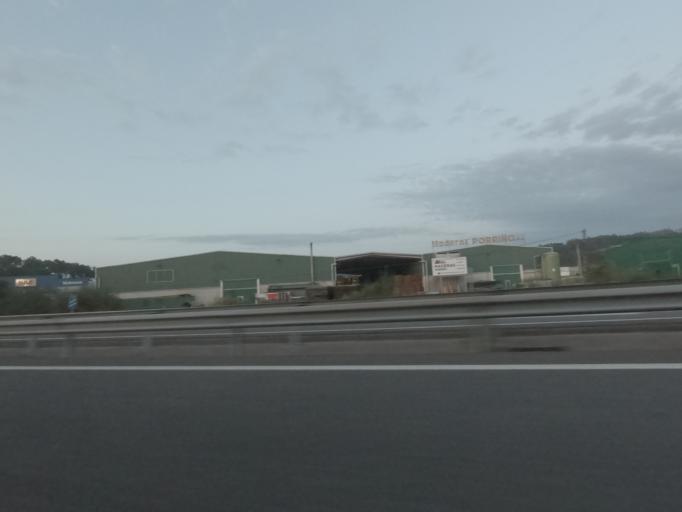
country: ES
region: Galicia
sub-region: Provincia de Pontevedra
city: Tui
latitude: 42.0893
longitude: -8.6267
